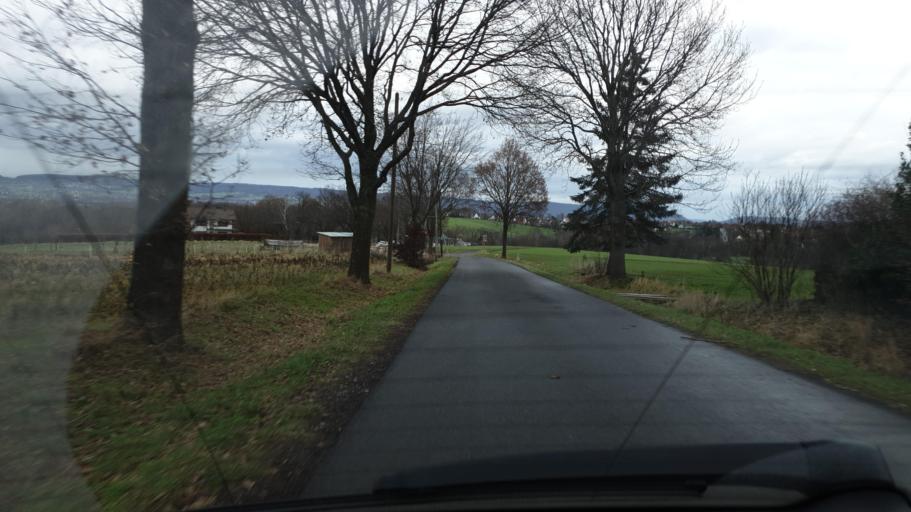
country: DE
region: North Rhine-Westphalia
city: Bad Oeynhausen
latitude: 52.1716
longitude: 8.7845
